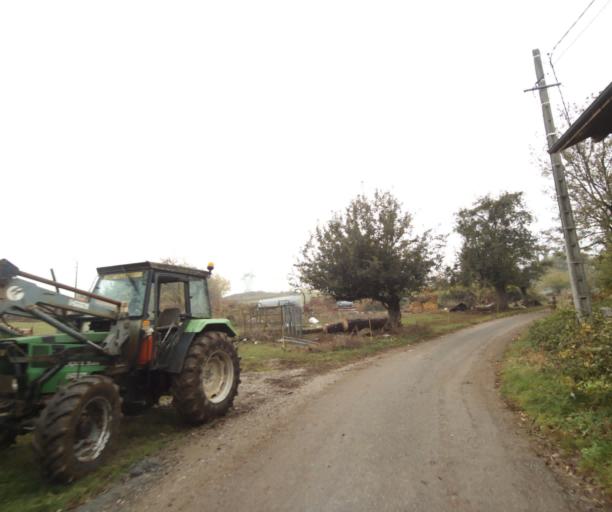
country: FR
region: Rhone-Alpes
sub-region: Departement de la Haute-Savoie
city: Reignier-Esery
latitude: 46.1392
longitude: 6.3006
